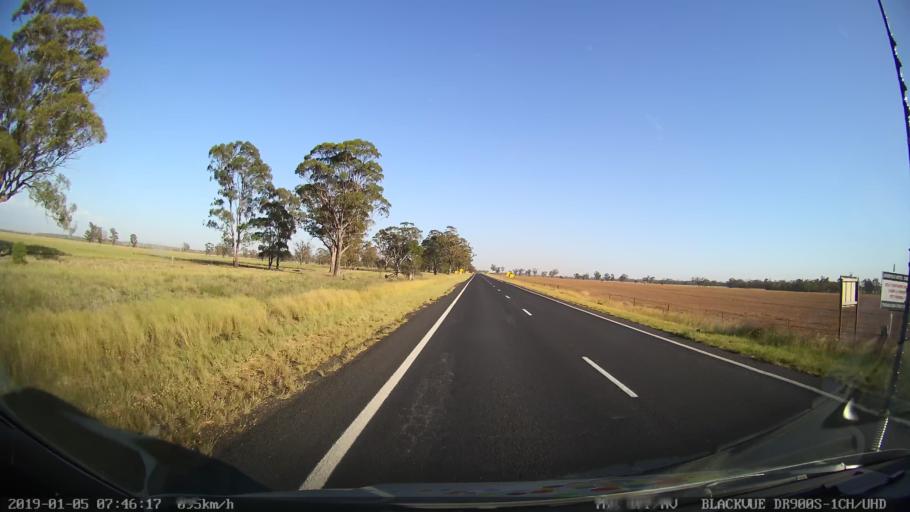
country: AU
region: New South Wales
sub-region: Gilgandra
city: Gilgandra
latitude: -31.8464
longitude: 148.6440
